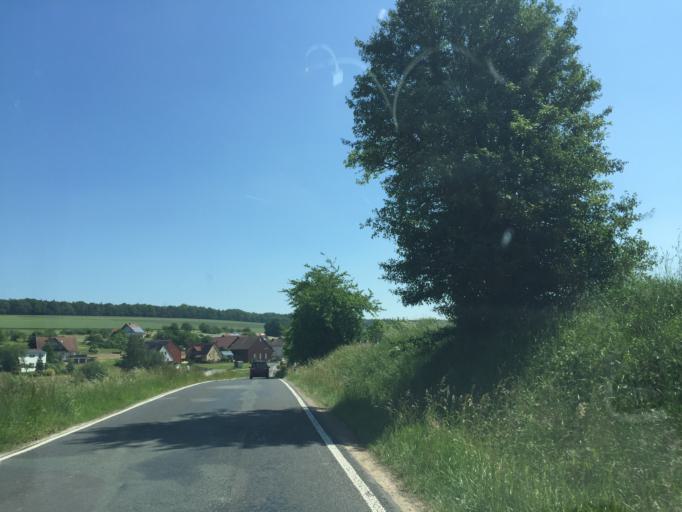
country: DE
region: Bavaria
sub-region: Regierungsbezirk Unterfranken
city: Miltenberg
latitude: 49.6585
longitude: 9.2769
